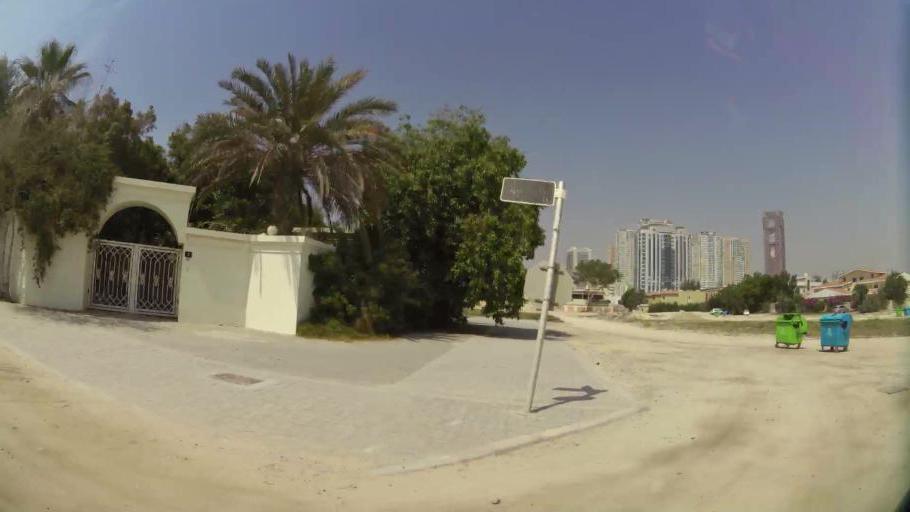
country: AE
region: Ajman
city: Ajman
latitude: 25.3929
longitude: 55.4231
